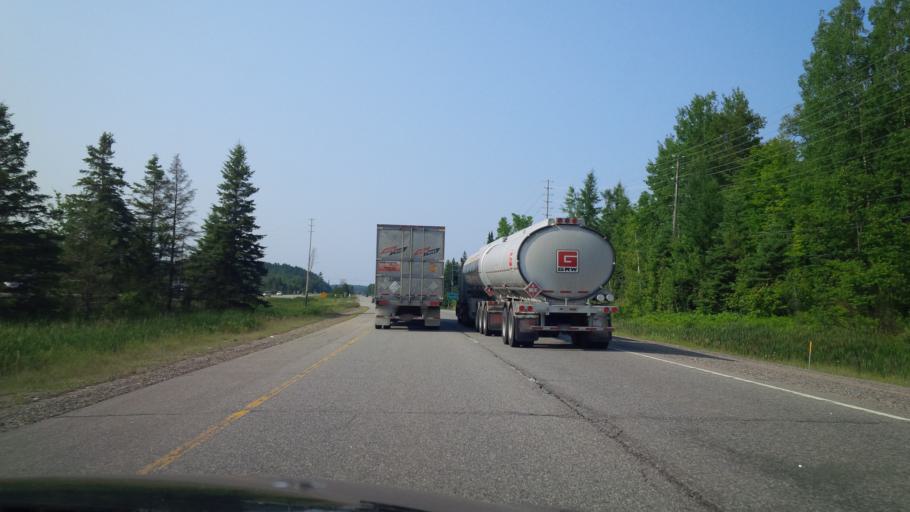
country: CA
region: Ontario
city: Huntsville
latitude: 45.2580
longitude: -79.2962
